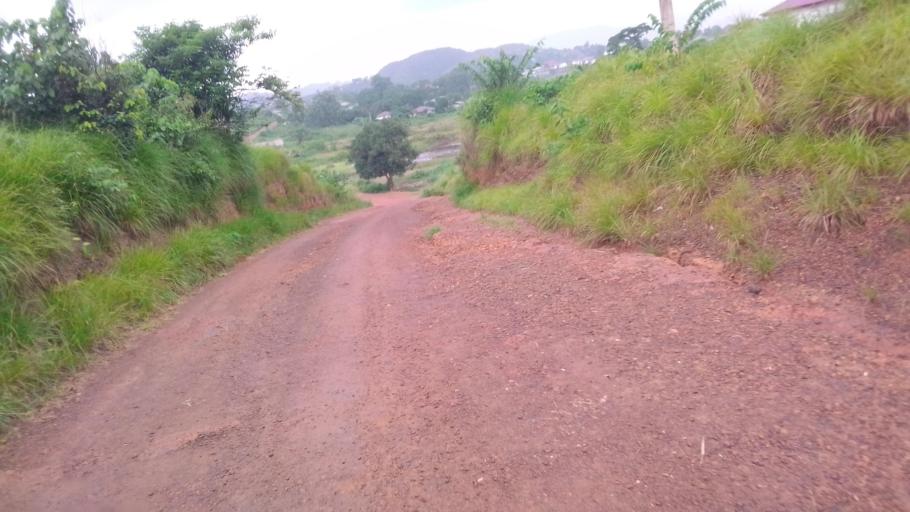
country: SL
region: Eastern Province
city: Kenema
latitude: 7.8406
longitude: -11.1775
